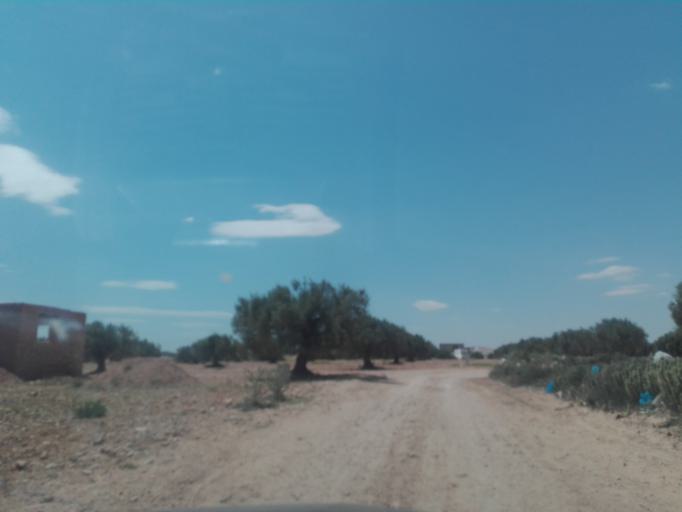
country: TN
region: Safaqis
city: Sfax
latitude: 34.6501
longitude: 10.5945
